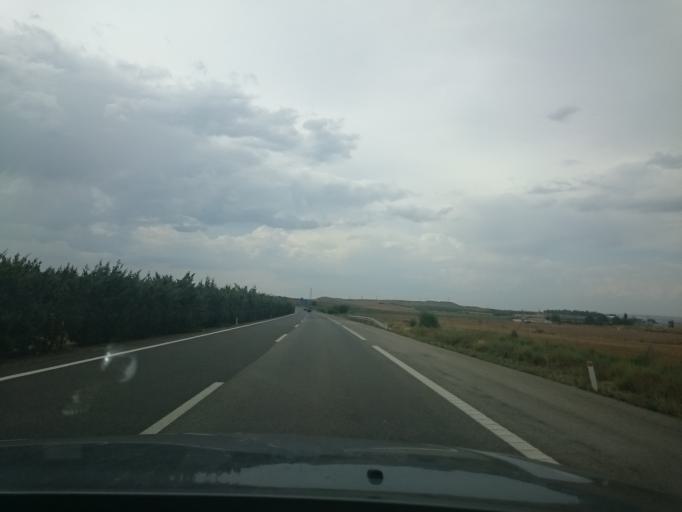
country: ES
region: Navarre
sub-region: Provincia de Navarra
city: Fontellas
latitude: 42.0037
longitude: -1.5855
